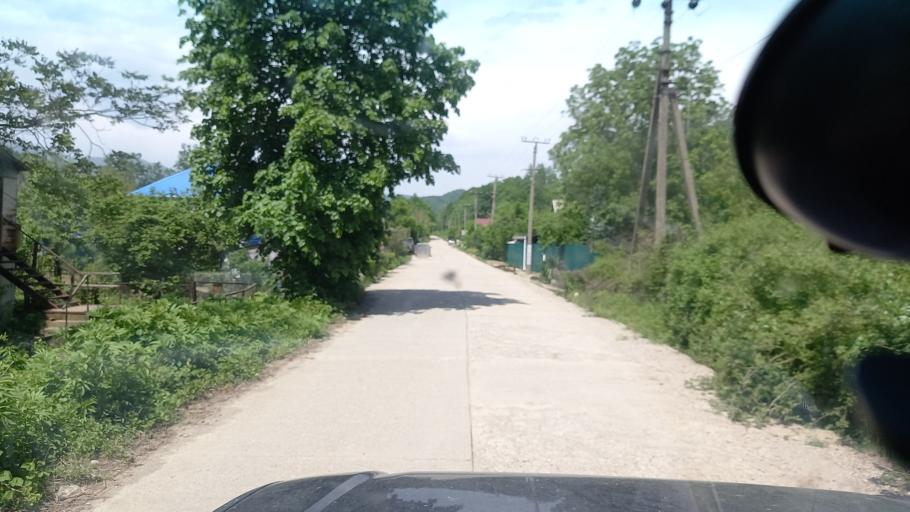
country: RU
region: Krasnodarskiy
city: Tuapse
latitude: 44.2428
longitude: 39.2402
